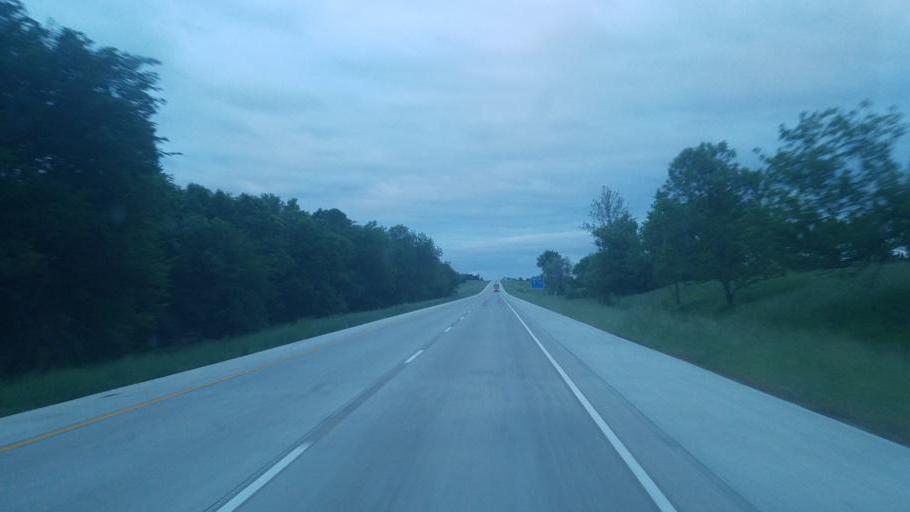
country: US
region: Iowa
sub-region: Decatur County
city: Lamoni
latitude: 40.6072
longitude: -93.9023
